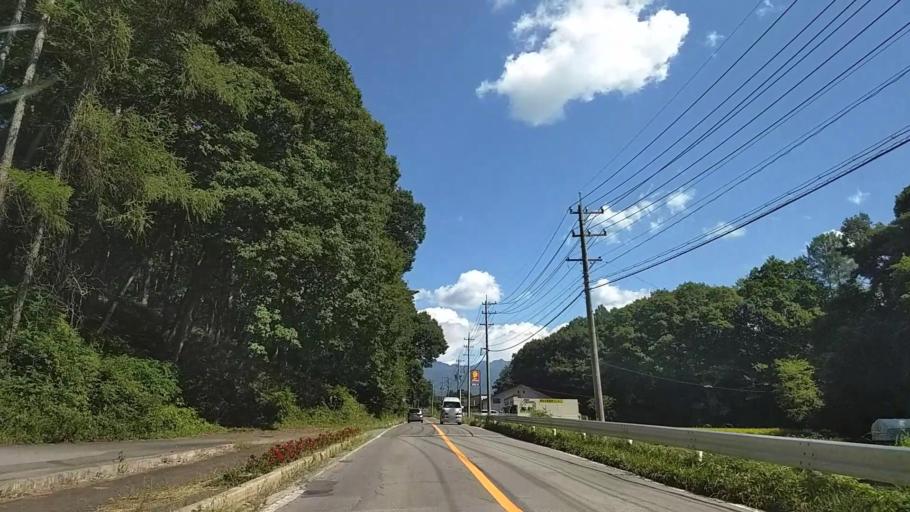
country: JP
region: Nagano
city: Chino
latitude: 36.0323
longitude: 138.2052
